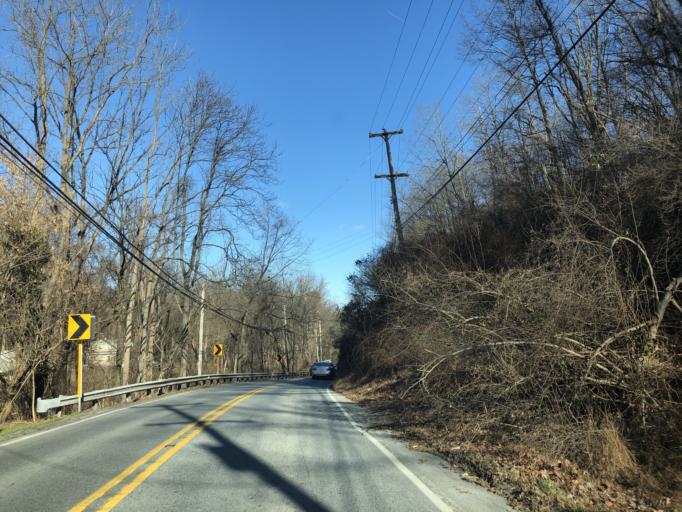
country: US
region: Pennsylvania
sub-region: Chester County
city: South Coatesville
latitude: 39.9686
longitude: -75.8334
